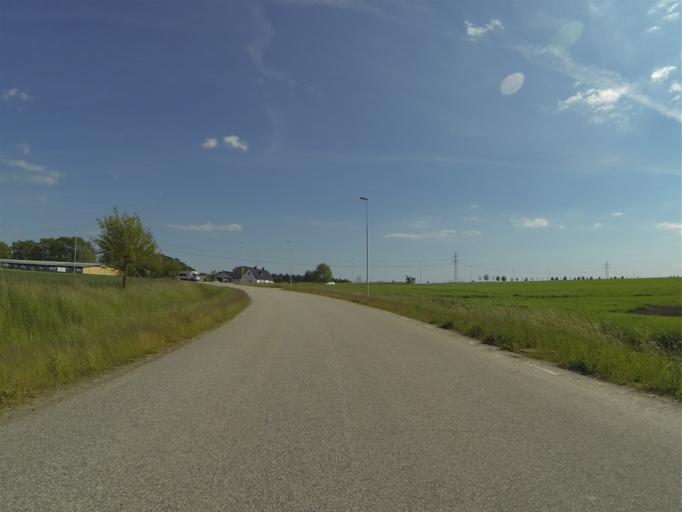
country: SE
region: Skane
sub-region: Burlovs Kommun
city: Arloev
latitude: 55.6347
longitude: 13.1138
